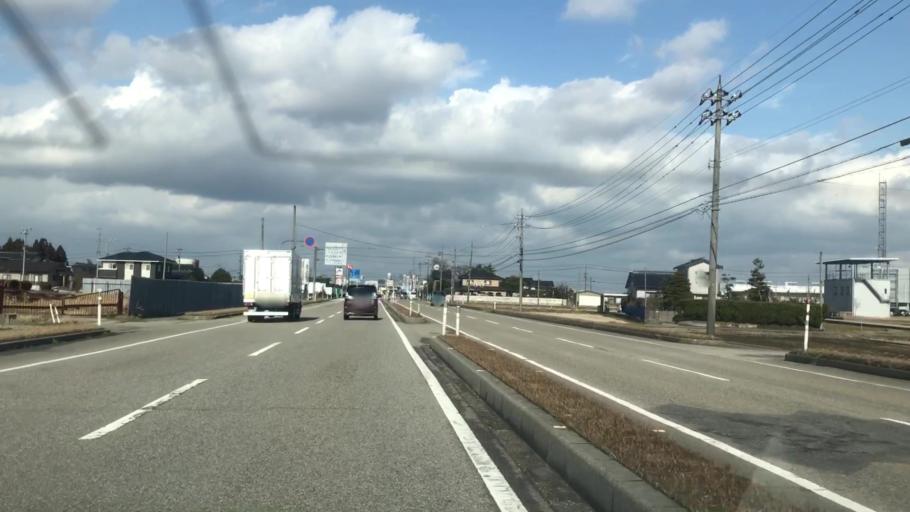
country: JP
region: Toyama
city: Kuragaki-kosugi
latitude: 36.7138
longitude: 137.0812
